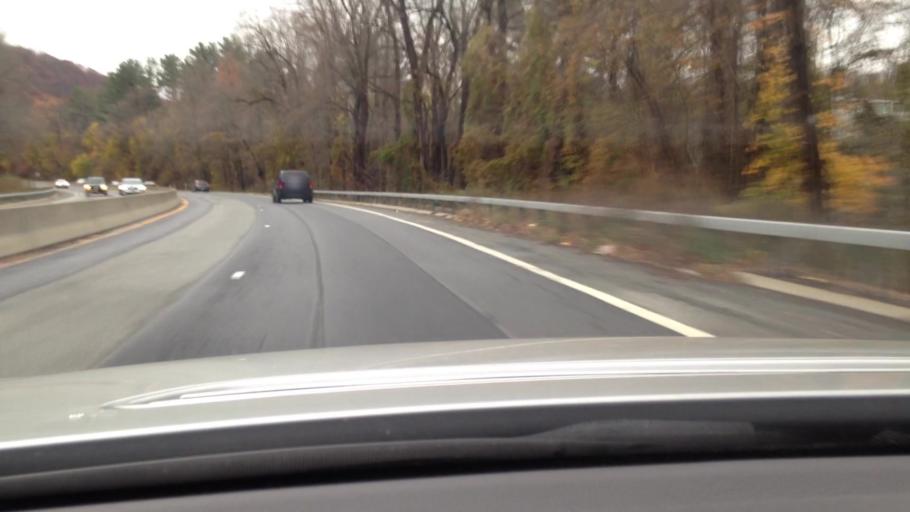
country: US
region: New York
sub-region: Westchester County
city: Hawthorne
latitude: 41.0981
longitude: -73.8110
